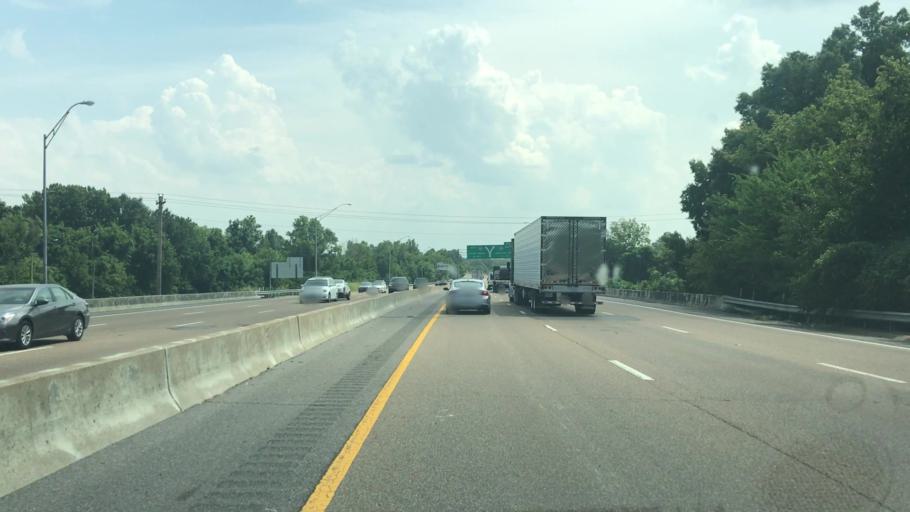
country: US
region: Tennessee
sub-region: Shelby County
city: Memphis
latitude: 35.1711
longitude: -90.0185
